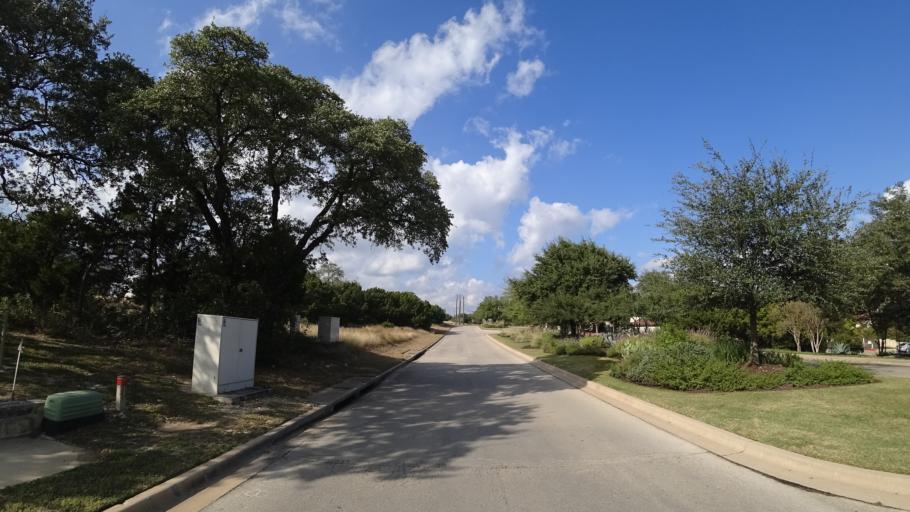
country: US
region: Texas
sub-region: Travis County
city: Barton Creek
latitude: 30.2894
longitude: -97.8728
